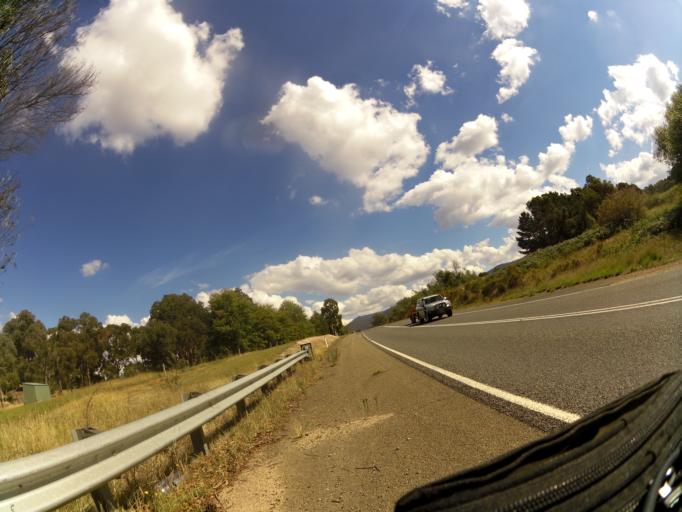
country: AU
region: Victoria
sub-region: Mansfield
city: Mansfield
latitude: -36.8531
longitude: 146.0060
